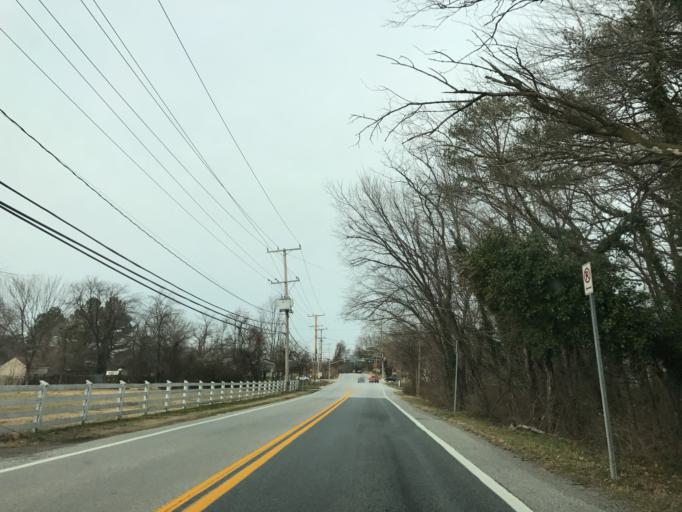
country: US
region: Maryland
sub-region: Anne Arundel County
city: Pasadena
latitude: 39.1097
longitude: -76.5550
